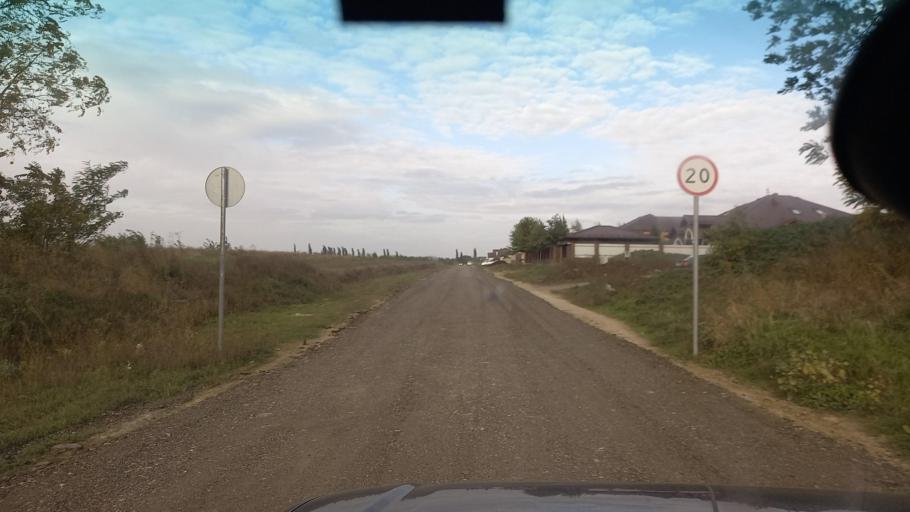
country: RU
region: Krasnodarskiy
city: Krasnodar
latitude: 45.1279
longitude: 38.9252
